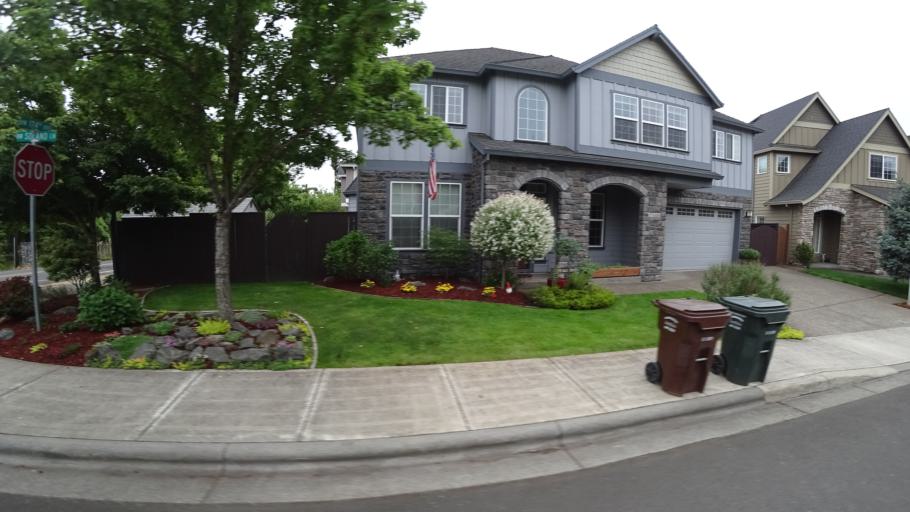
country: US
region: Oregon
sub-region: Washington County
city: Bethany
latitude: 45.5524
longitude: -122.8576
